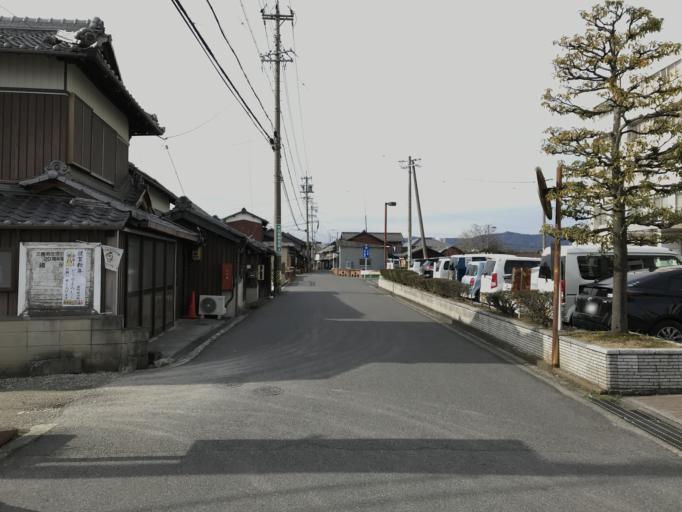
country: JP
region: Mie
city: Ueno-ebisumachi
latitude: 34.7568
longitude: 136.1365
